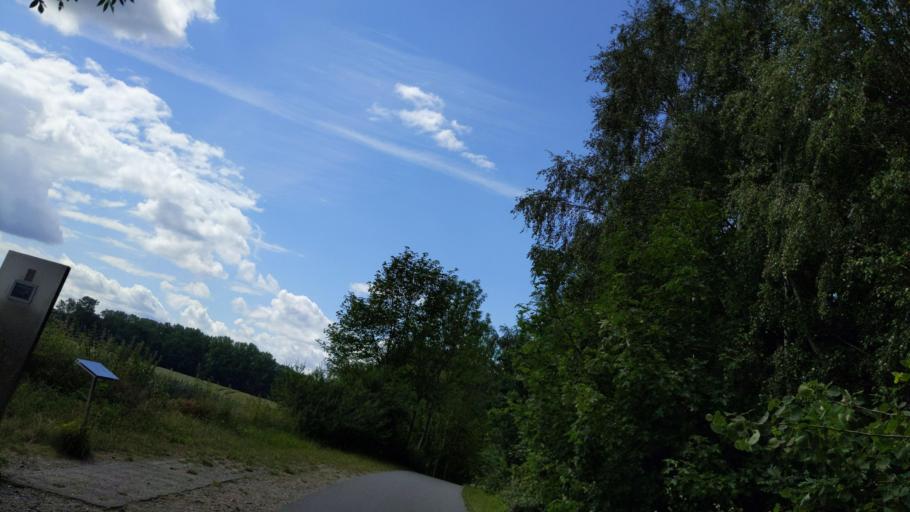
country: DE
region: Mecklenburg-Vorpommern
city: Klutz
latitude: 54.0110
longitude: 11.1119
